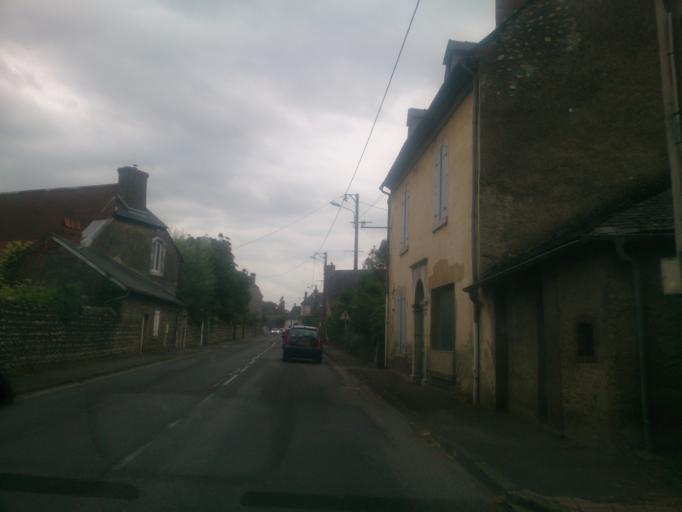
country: FR
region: Midi-Pyrenees
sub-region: Departement des Hautes-Pyrenees
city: Horgues
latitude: 43.1895
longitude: 0.0866
